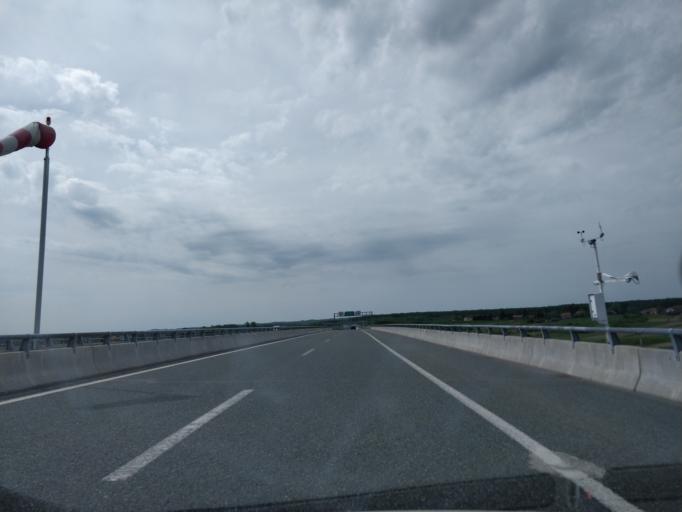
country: HR
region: Zagrebacka
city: Mraclin
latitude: 45.6767
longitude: 16.0802
